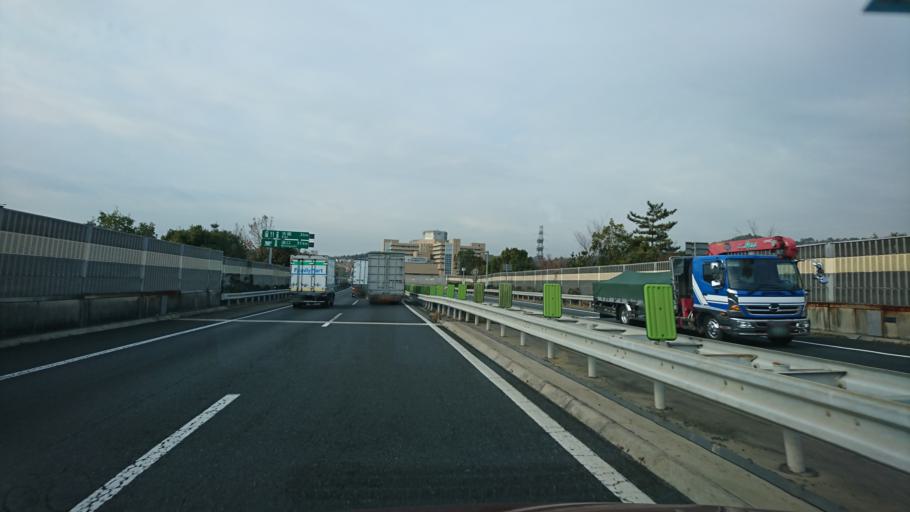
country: JP
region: Okayama
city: Okayama-shi
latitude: 34.7084
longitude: 133.9054
